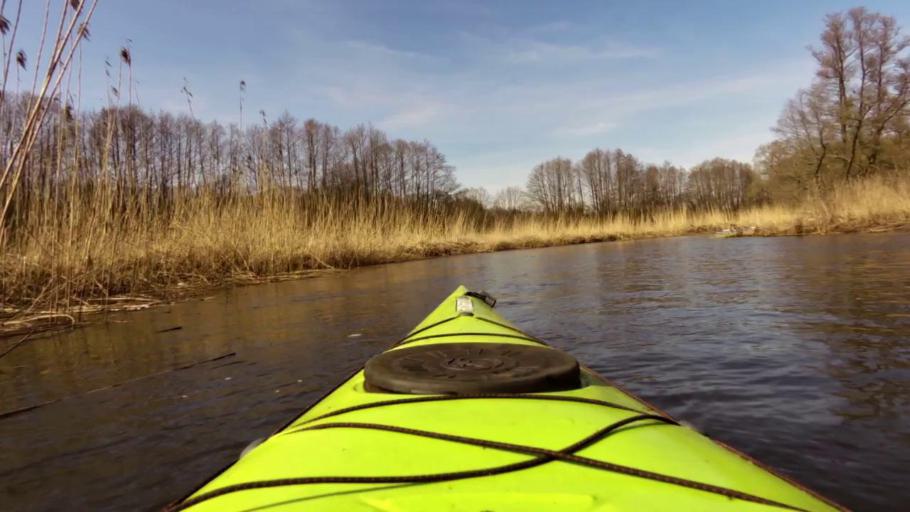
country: PL
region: West Pomeranian Voivodeship
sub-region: Powiat lobeski
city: Lobez
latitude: 53.6676
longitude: 15.5642
